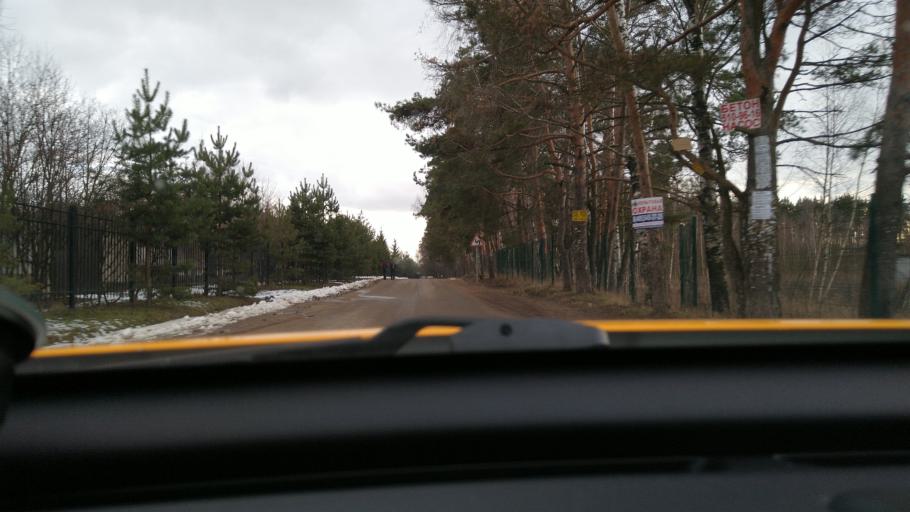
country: RU
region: Moskovskaya
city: Petrovo-Dal'neye
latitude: 55.7635
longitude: 37.2054
